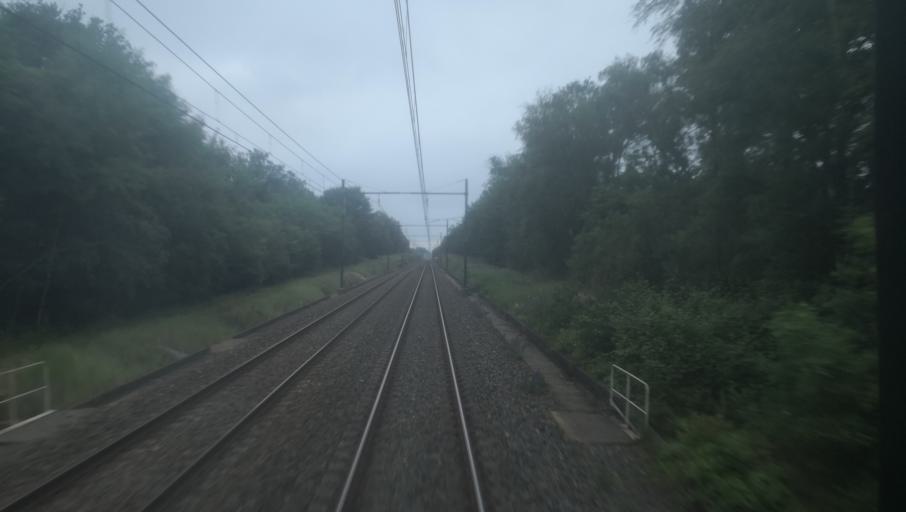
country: FR
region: Centre
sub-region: Departement du Loir-et-Cher
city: Theillay
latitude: 47.3564
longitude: 2.0475
